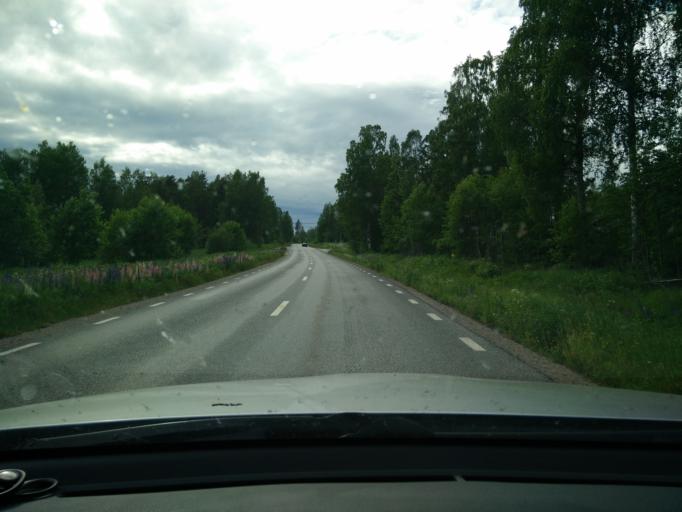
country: SE
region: Gaevleborg
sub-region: Nordanstigs Kommun
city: Bergsjoe
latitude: 62.0845
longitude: 16.7997
